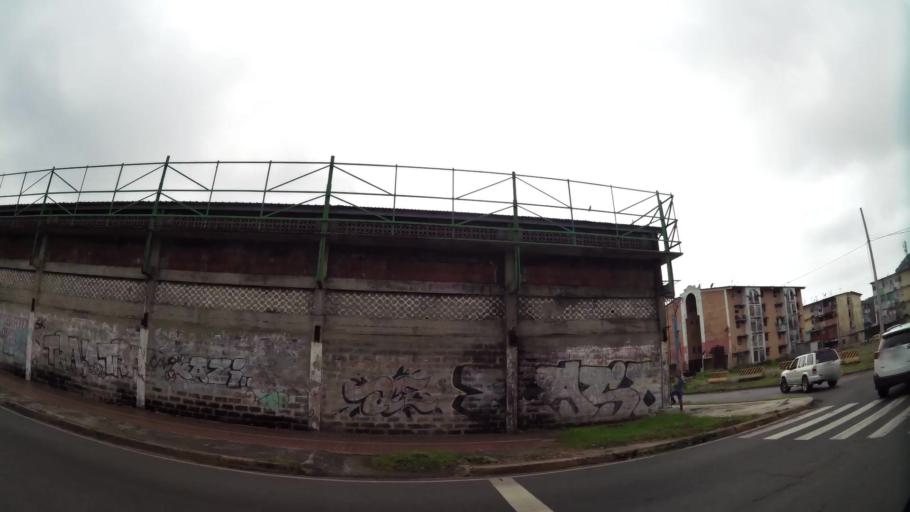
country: PA
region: Panama
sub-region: Distrito de Panama
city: Ancon
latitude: 8.9673
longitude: -79.5436
